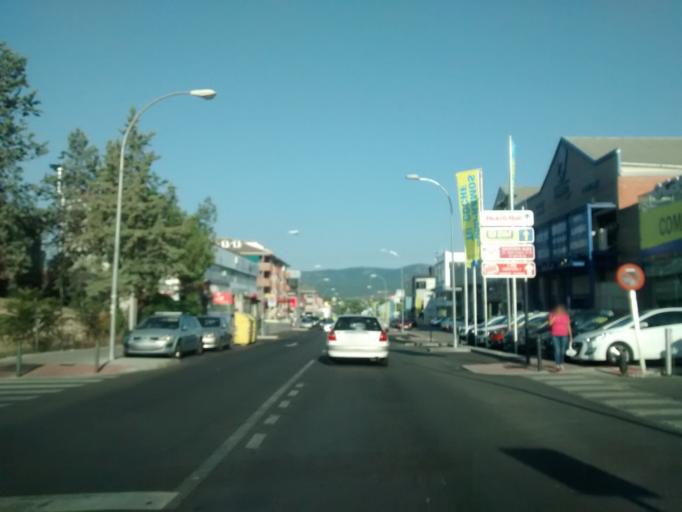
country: ES
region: Madrid
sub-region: Provincia de Madrid
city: Collado-Villalba
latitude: 40.6337
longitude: -4.0069
